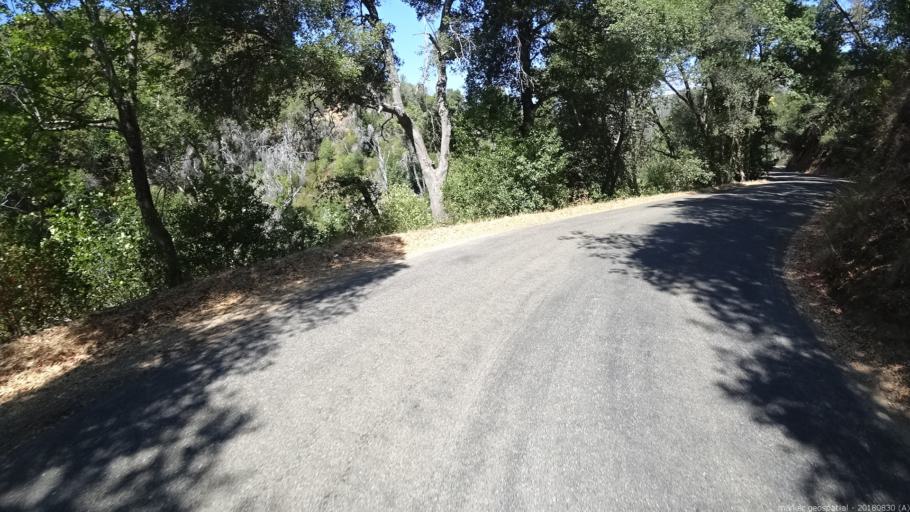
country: US
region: California
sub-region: Monterey County
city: Greenfield
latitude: 36.0108
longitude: -121.4356
